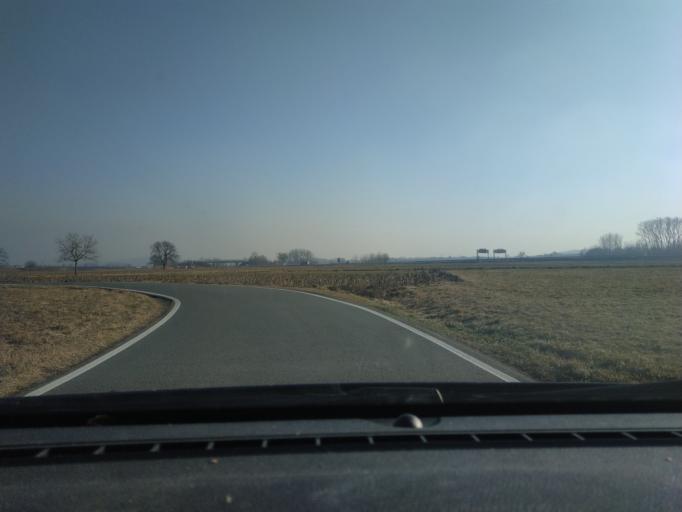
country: IT
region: Piedmont
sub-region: Provincia di Torino
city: Pavone Canavese
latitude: 45.4267
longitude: 7.8636
